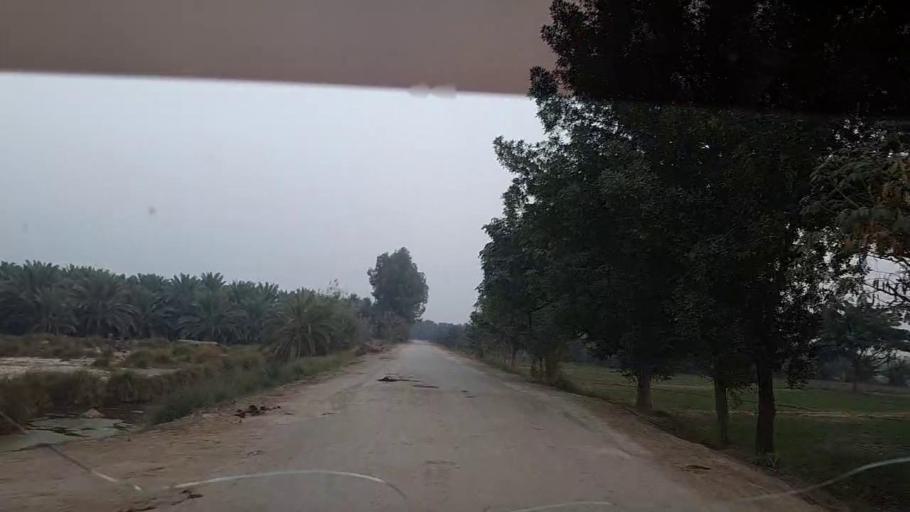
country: PK
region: Sindh
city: Khairpur
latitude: 27.5749
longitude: 68.7231
